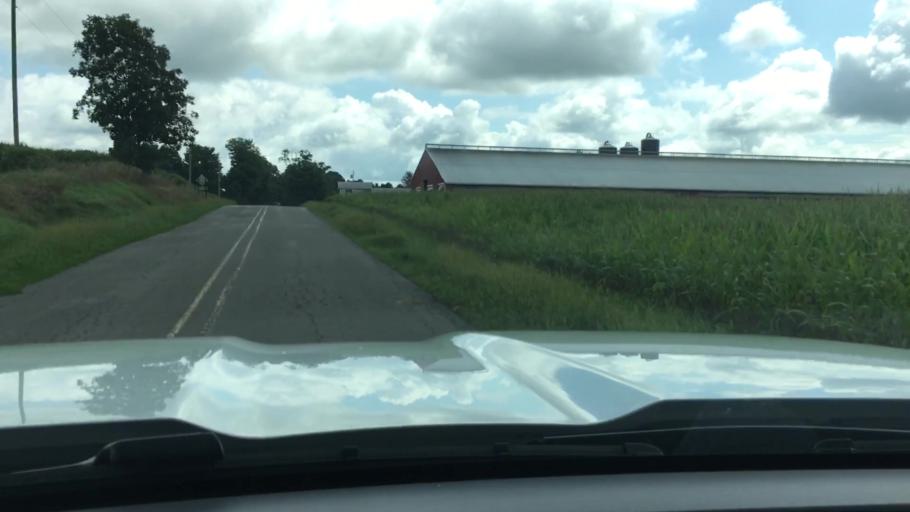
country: US
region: Michigan
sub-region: Ingham County
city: Holt
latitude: 42.5385
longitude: -84.5416
